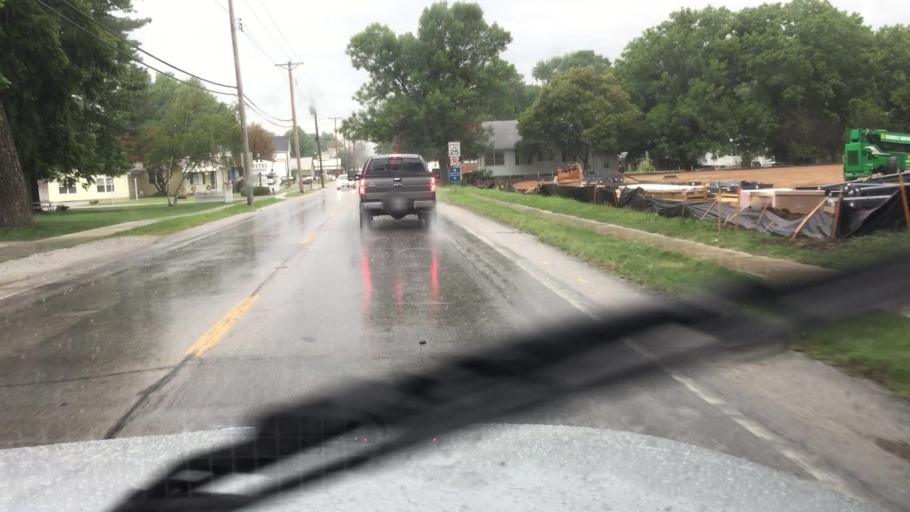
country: US
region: Illinois
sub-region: Hancock County
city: Nauvoo
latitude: 40.5497
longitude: -91.3757
